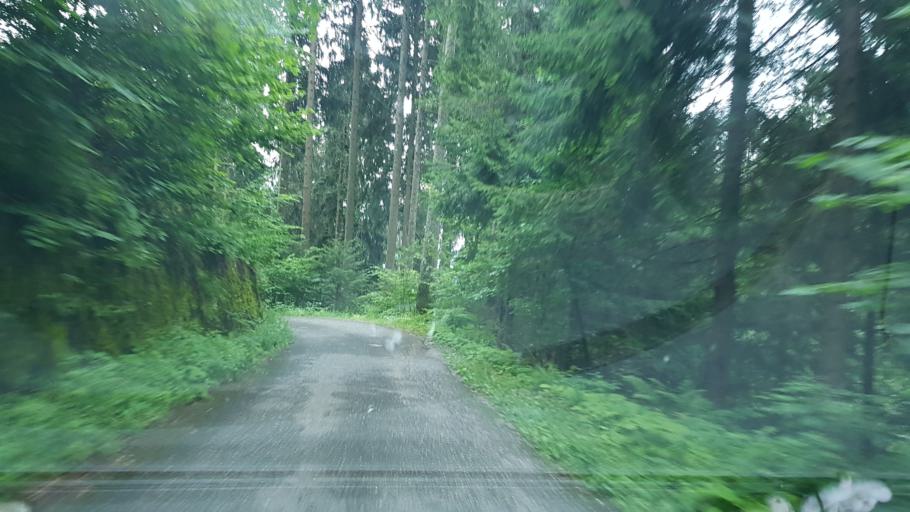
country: IT
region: Friuli Venezia Giulia
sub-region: Provincia di Udine
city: Cercivento
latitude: 46.5366
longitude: 12.9867
